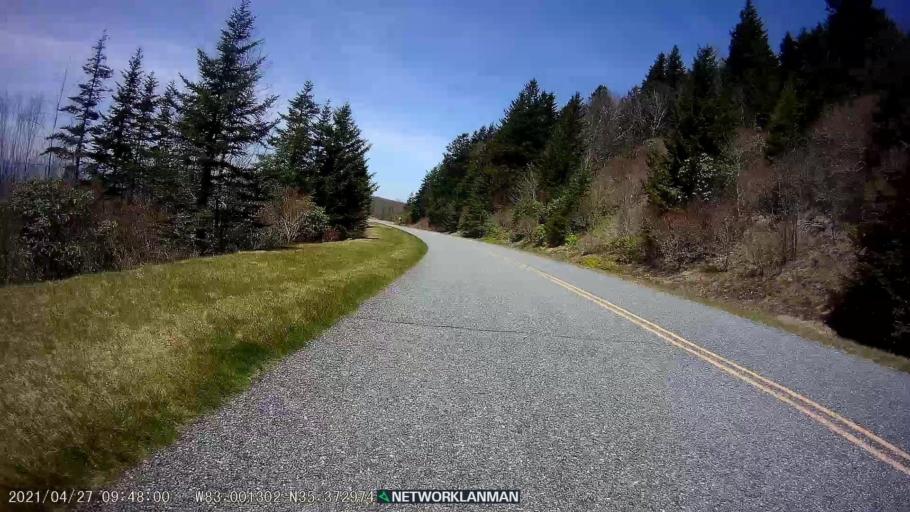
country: US
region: North Carolina
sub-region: Haywood County
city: Hazelwood
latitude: 35.3726
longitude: -83.0010
